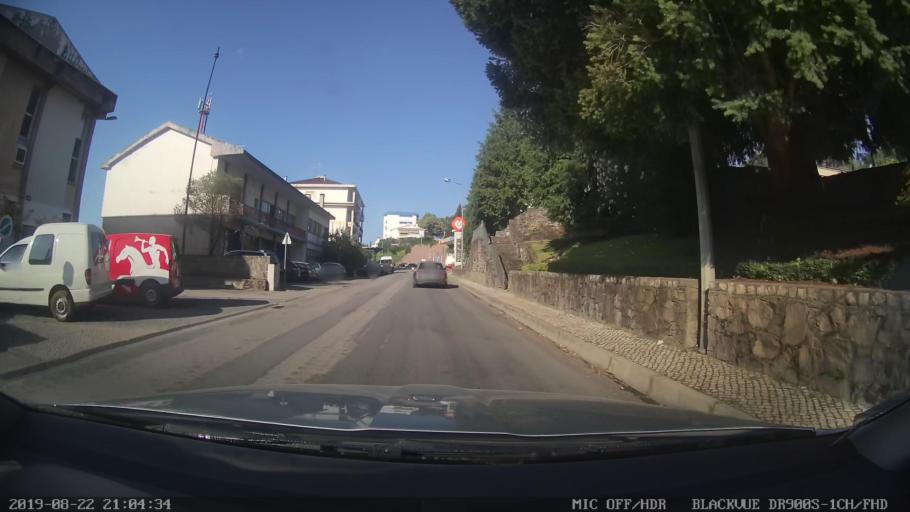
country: PT
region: Castelo Branco
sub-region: Serta
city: Serta
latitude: 39.8039
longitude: -8.1004
